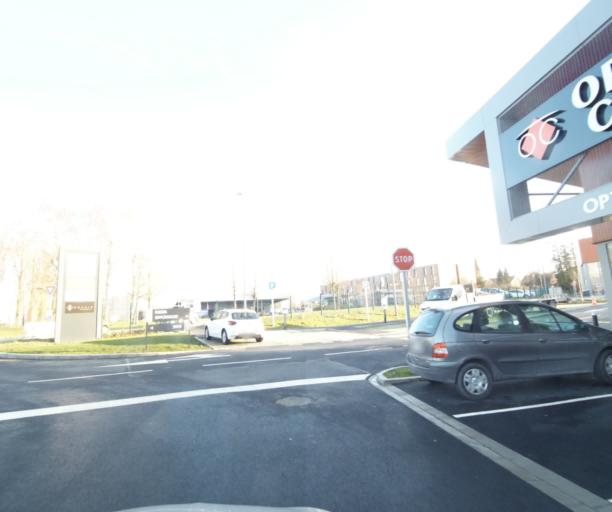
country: FR
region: Nord-Pas-de-Calais
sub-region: Departement du Nord
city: Famars
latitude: 50.3336
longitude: 3.5102
